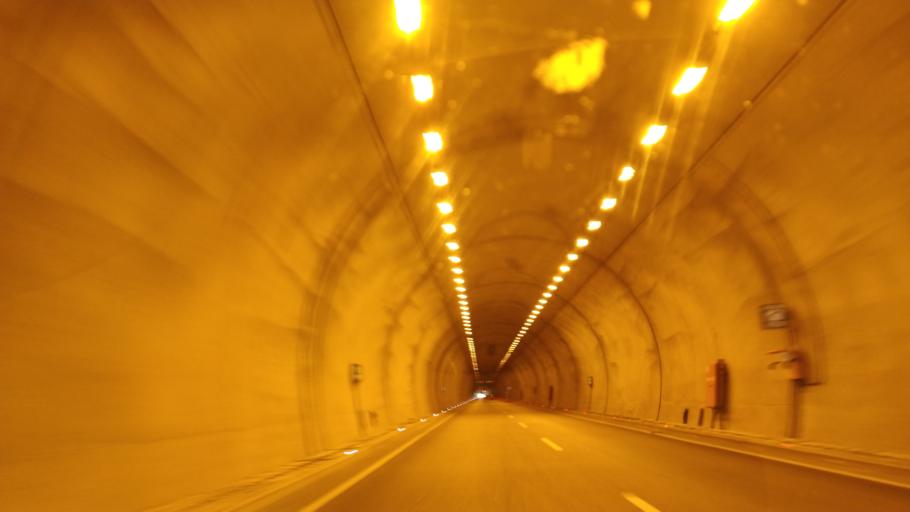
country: TR
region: Mersin
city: Akdere
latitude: 36.2585
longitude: 33.7931
